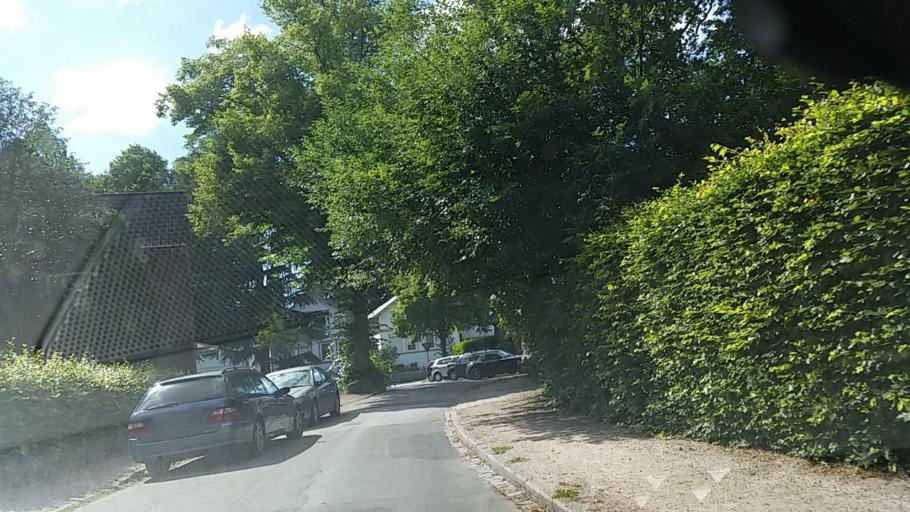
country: DE
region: Schleswig-Holstein
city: Halstenbek
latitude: 53.5558
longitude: 9.8457
